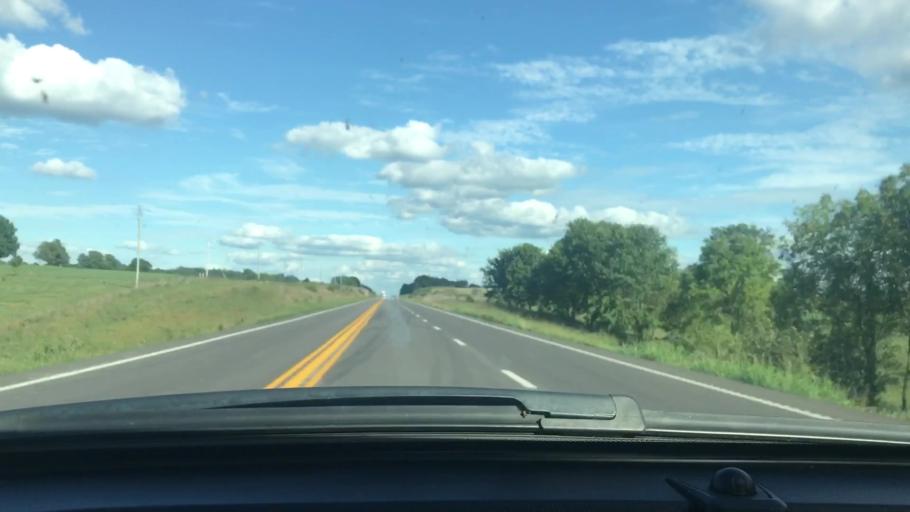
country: US
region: Missouri
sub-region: Oregon County
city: Thayer
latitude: 36.5856
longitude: -91.6239
